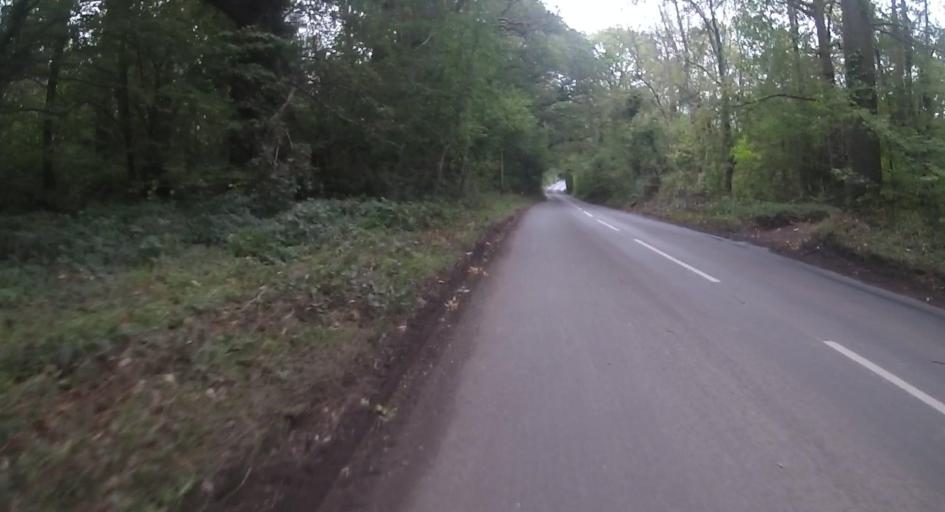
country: GB
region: England
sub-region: Hampshire
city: Fleet
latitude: 51.2500
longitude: -0.8623
